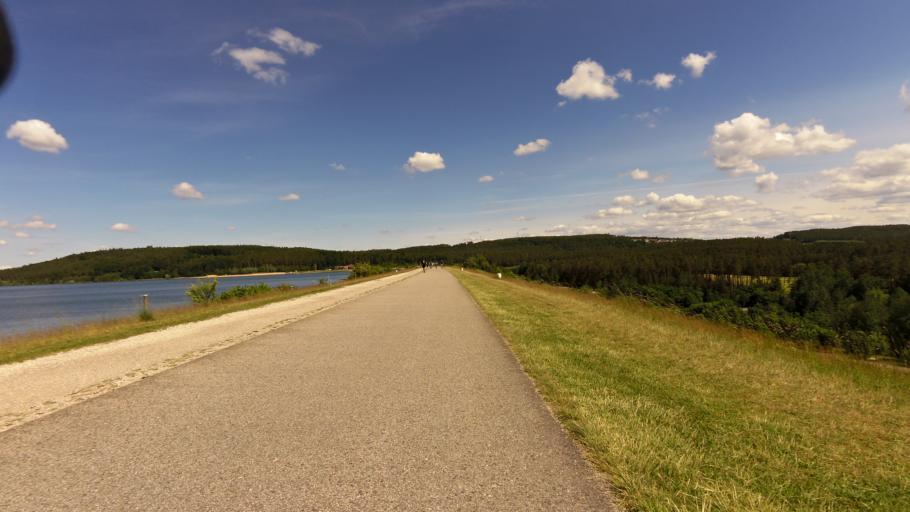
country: DE
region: Bavaria
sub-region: Regierungsbezirk Mittelfranken
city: Pleinfeld
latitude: 49.1253
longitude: 10.9642
